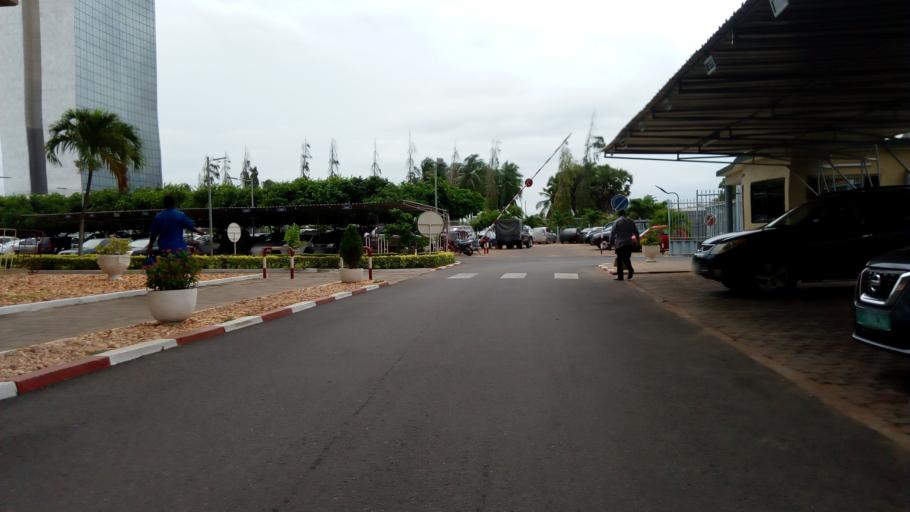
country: TG
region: Maritime
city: Lome
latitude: 6.1285
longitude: 1.2175
